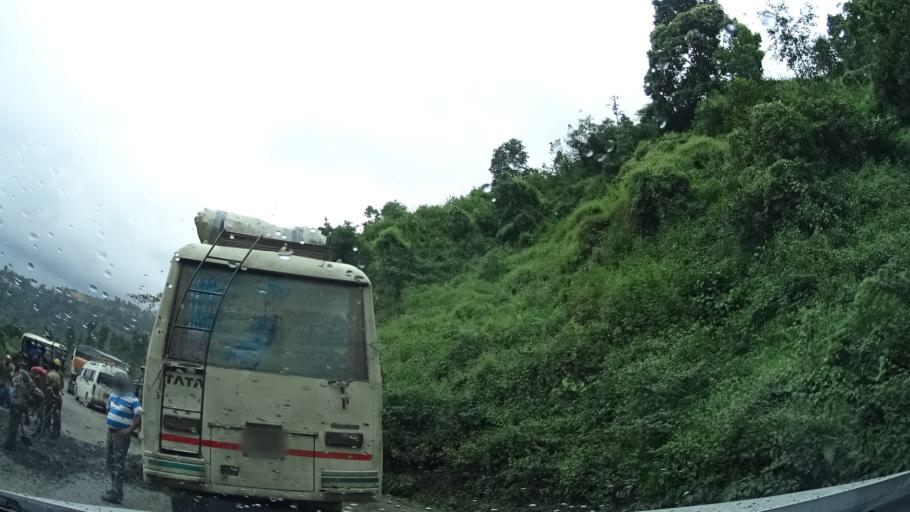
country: NP
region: Central Region
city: Kirtipur
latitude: 27.7090
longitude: 85.1915
